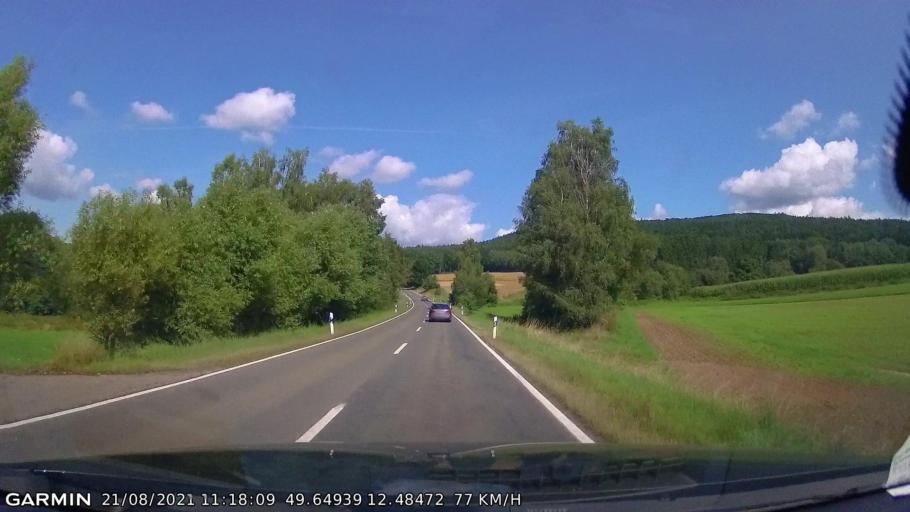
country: DE
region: Bavaria
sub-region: Upper Palatinate
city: Waidhaus
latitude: 49.6496
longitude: 12.4846
